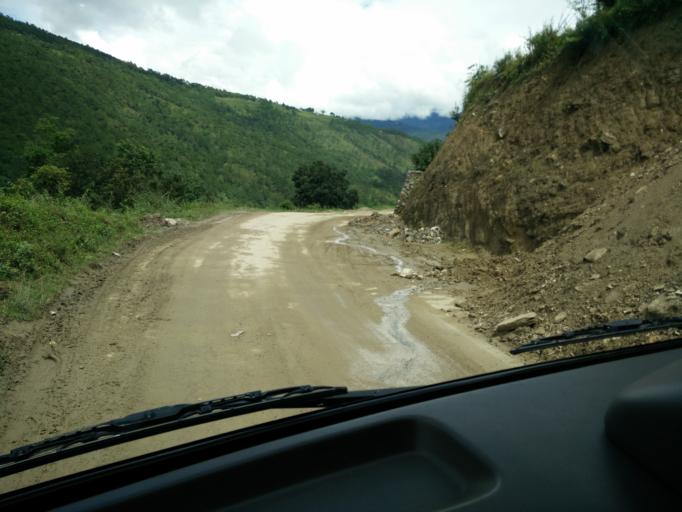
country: BT
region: Punakha
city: Pajo
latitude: 27.5268
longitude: 89.8300
